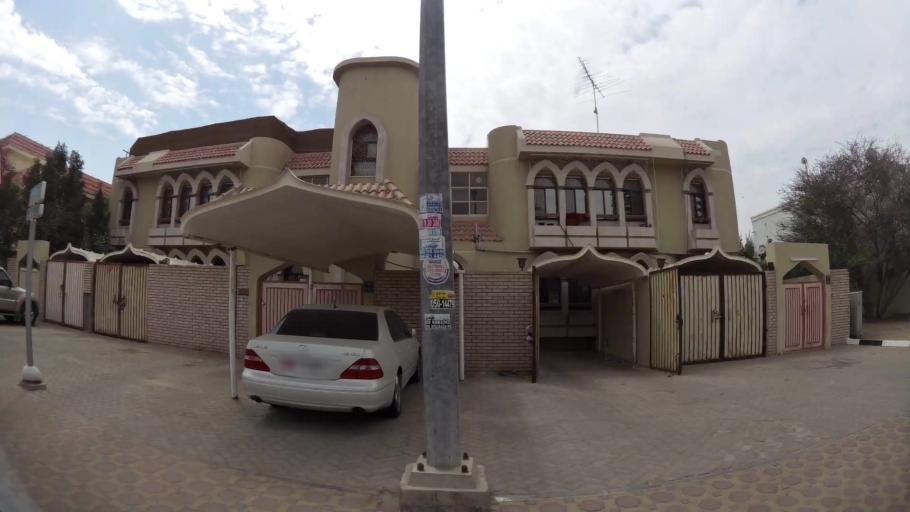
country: OM
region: Al Buraimi
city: Al Buraymi
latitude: 24.2244
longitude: 55.7871
